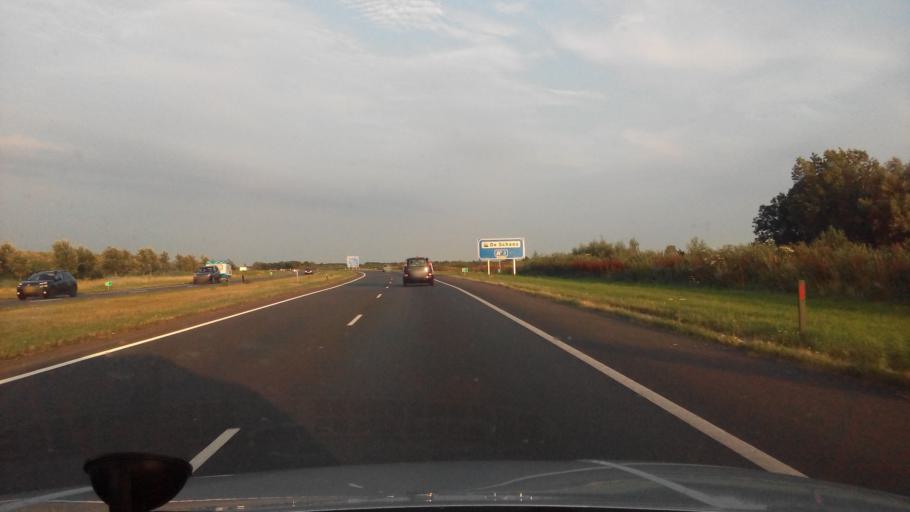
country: NL
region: South Holland
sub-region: Gemeente Alphen aan den Rijn
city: Alphen aan den Rijn
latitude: 52.1139
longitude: 4.6378
